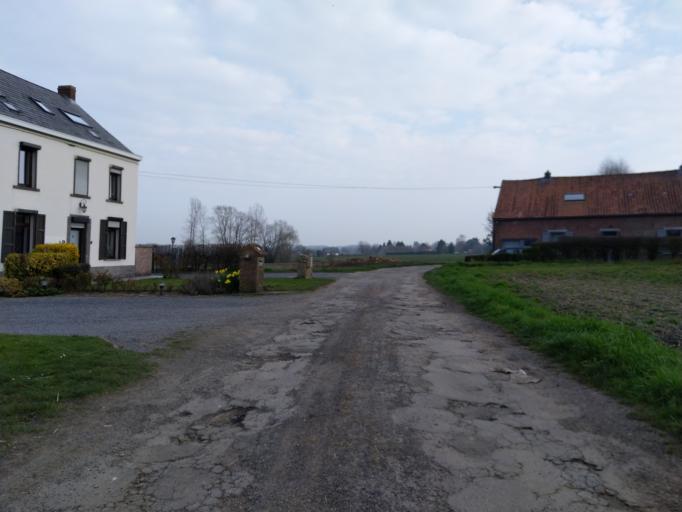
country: BE
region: Wallonia
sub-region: Province du Hainaut
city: Mons
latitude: 50.5214
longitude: 4.0004
